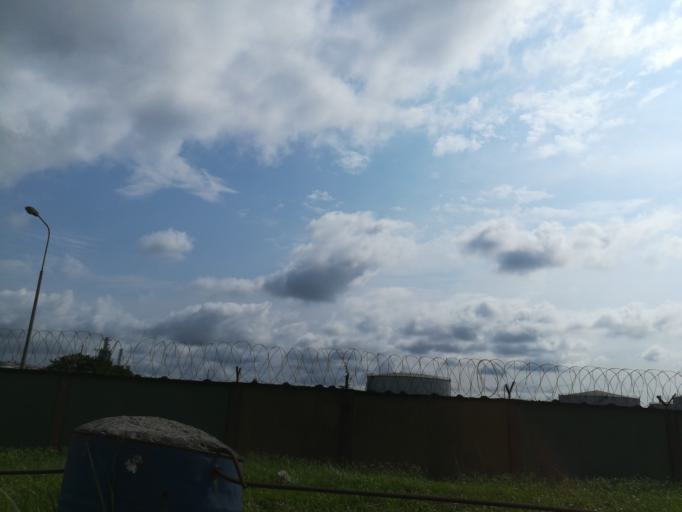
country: NG
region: Rivers
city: Okrika
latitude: 4.7612
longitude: 7.0970
